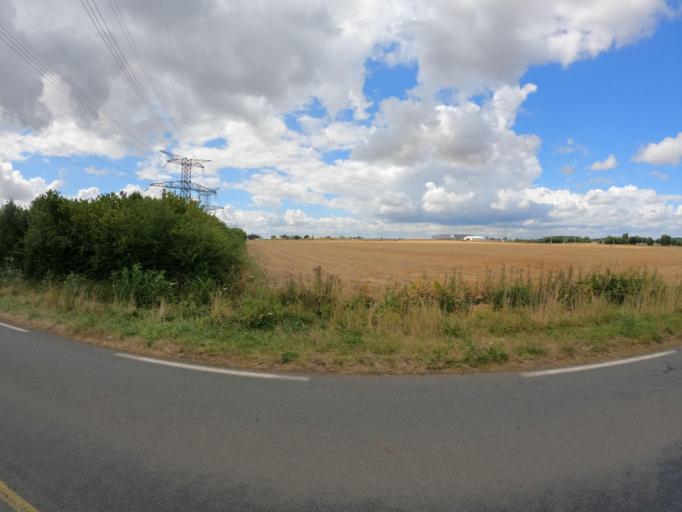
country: FR
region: Pays de la Loire
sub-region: Departement de la Sarthe
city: Juigne-sur-Sarthe
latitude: 47.8765
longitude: -0.3040
